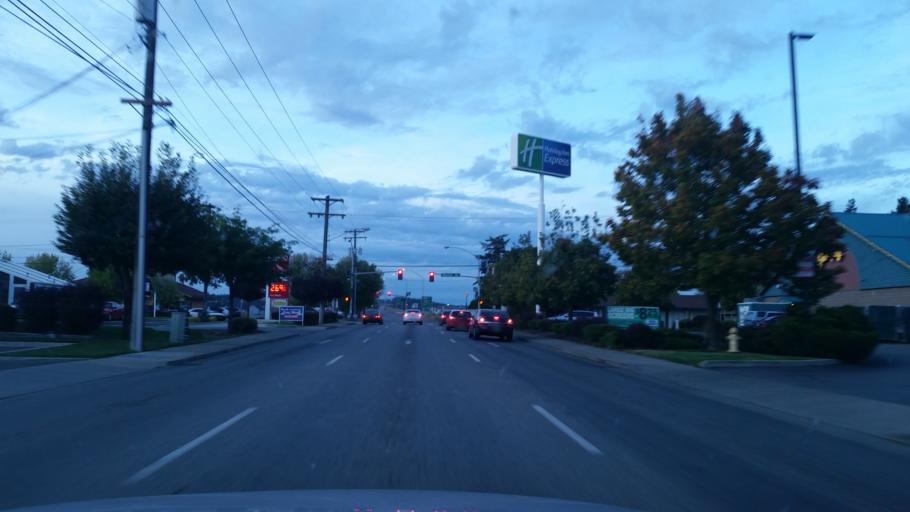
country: US
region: Washington
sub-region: Spokane County
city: Millwood
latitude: 47.6707
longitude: -117.2816
